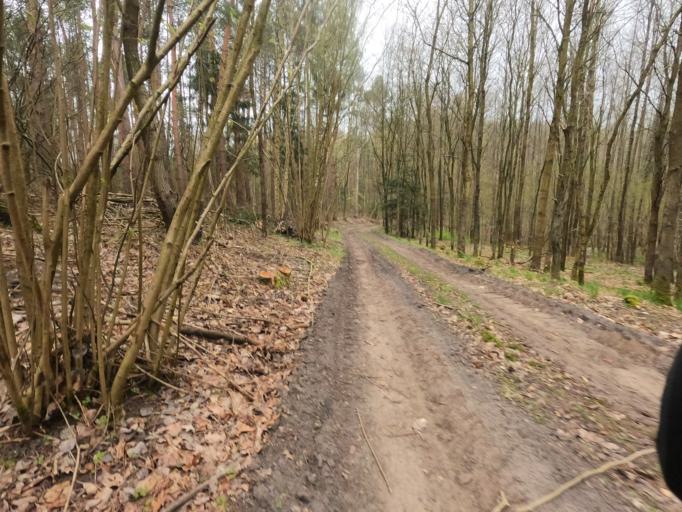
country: PL
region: West Pomeranian Voivodeship
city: Trzcinsko Zdroj
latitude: 52.9177
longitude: 14.6129
